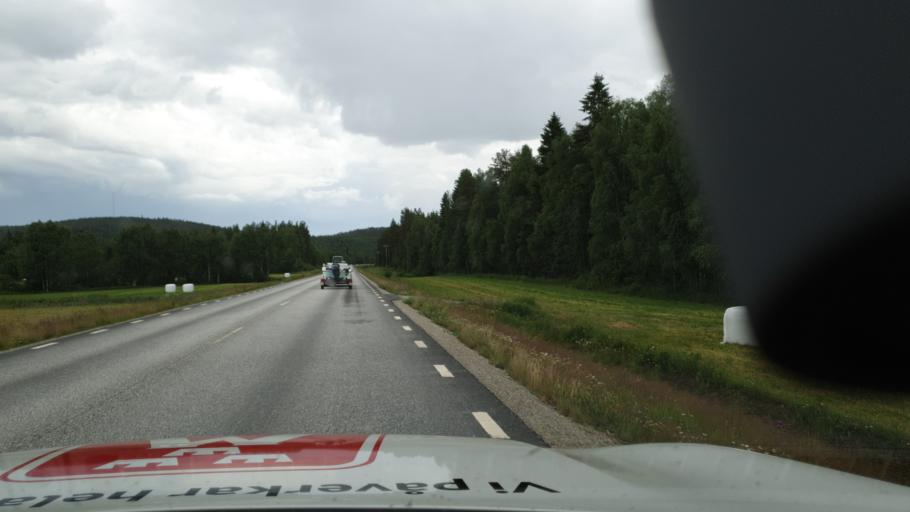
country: SE
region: Vaesterbotten
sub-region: Vindelns Kommun
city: Vindeln
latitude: 64.0494
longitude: 19.6767
